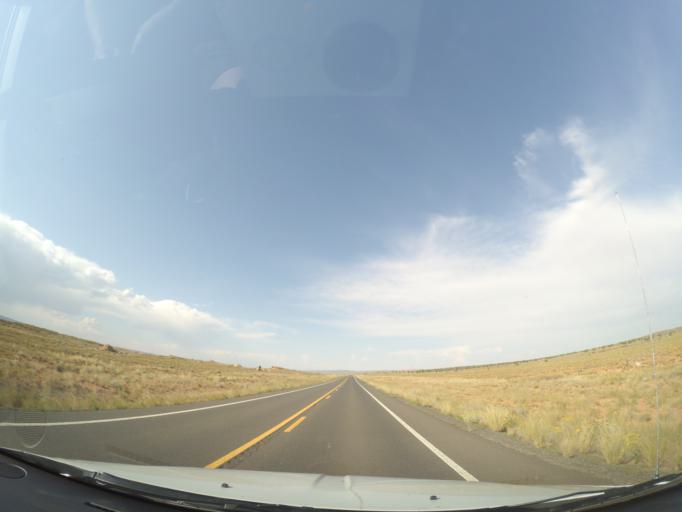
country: US
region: Arizona
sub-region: Coconino County
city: Tuba City
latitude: 36.3476
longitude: -111.4268
